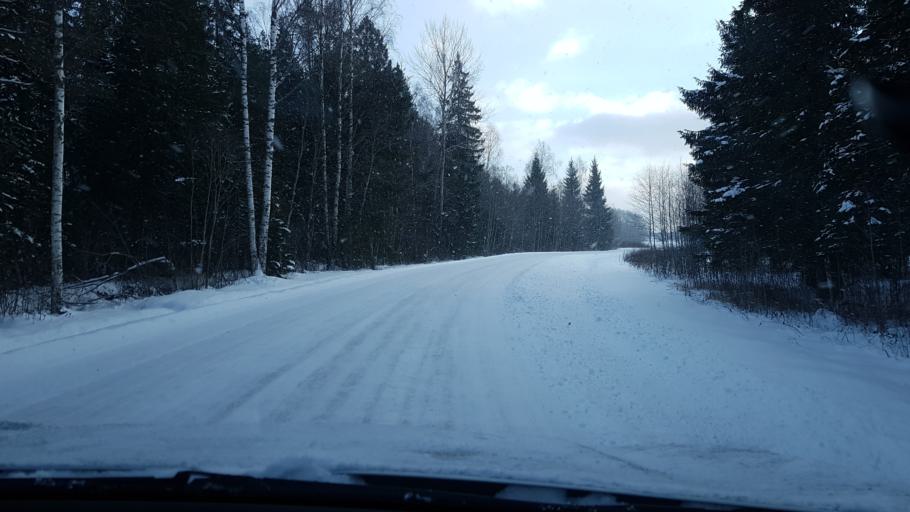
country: EE
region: Harju
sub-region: Nissi vald
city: Turba
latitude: 59.1715
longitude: 24.1366
